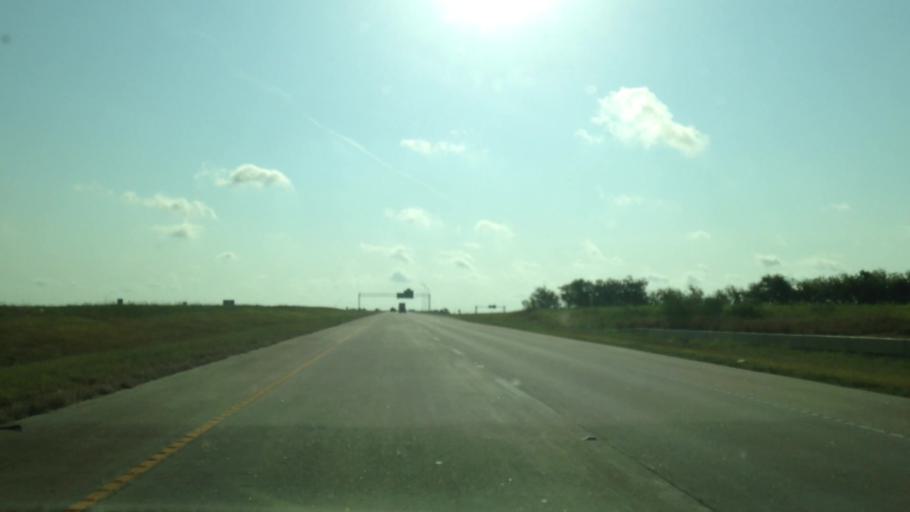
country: US
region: Texas
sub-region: Travis County
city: Onion Creek
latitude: 30.0814
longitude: -97.7173
